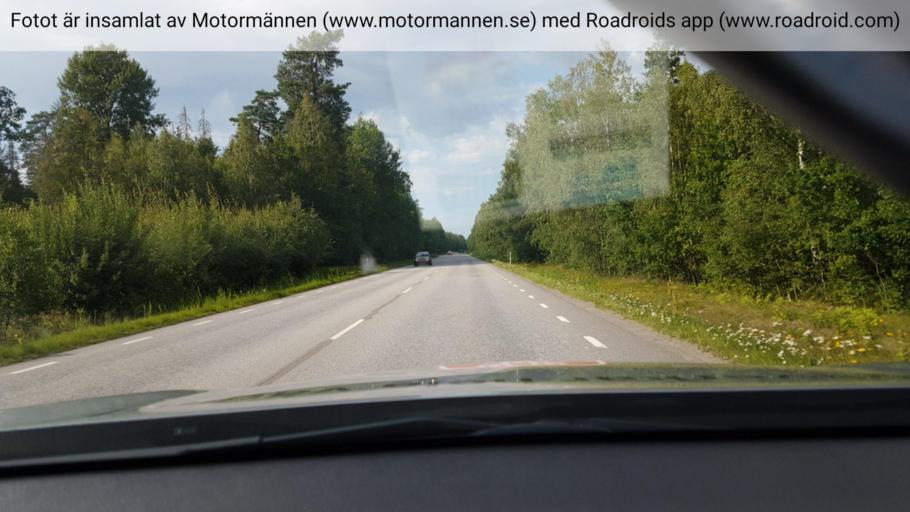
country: SE
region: Vaestra Goetaland
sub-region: Lidkopings Kommun
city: Lidkoping
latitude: 58.5236
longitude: 13.1126
